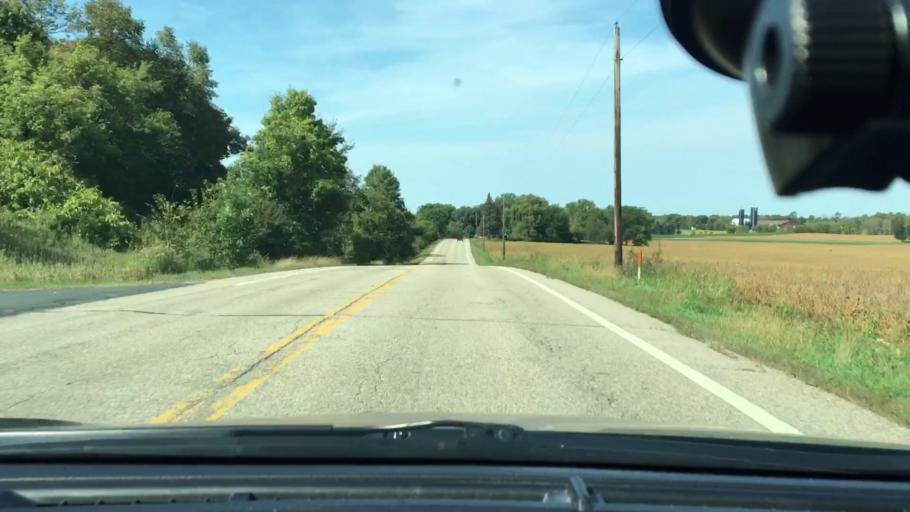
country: US
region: Minnesota
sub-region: Hennepin County
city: Corcoran
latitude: 45.1178
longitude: -93.5949
